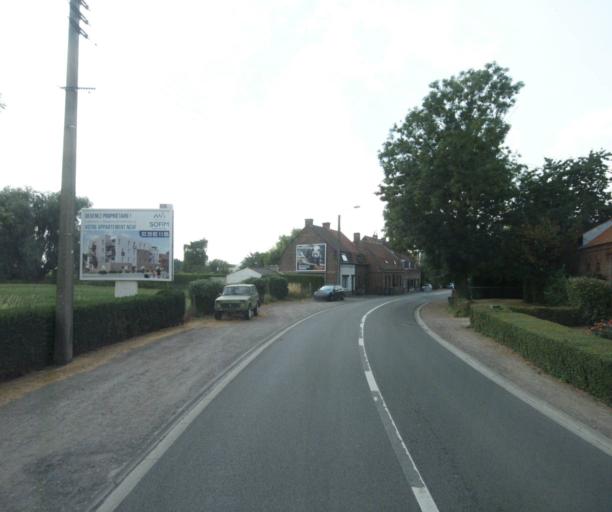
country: FR
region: Nord-Pas-de-Calais
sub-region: Departement du Nord
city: Linselles
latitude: 50.7407
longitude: 3.0686
